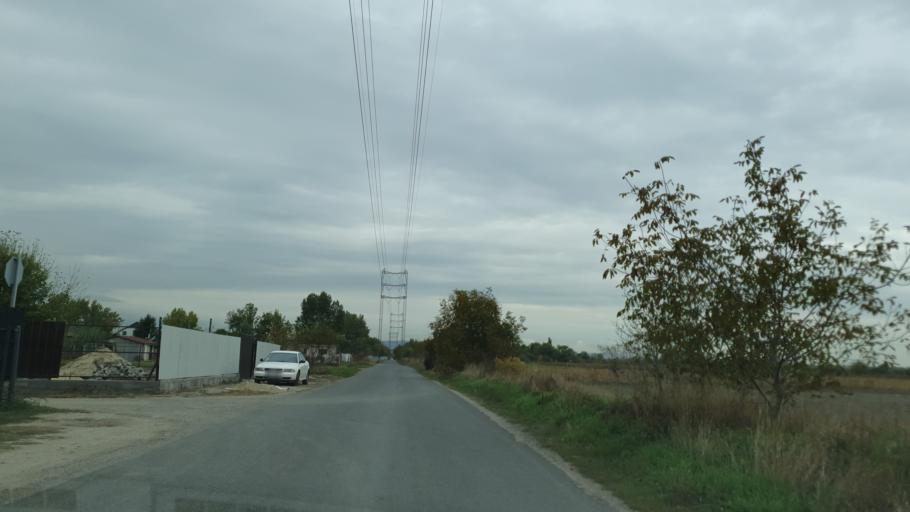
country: HU
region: Budapest
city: Budapest XXI. keruelet
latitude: 47.3929
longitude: 19.0685
